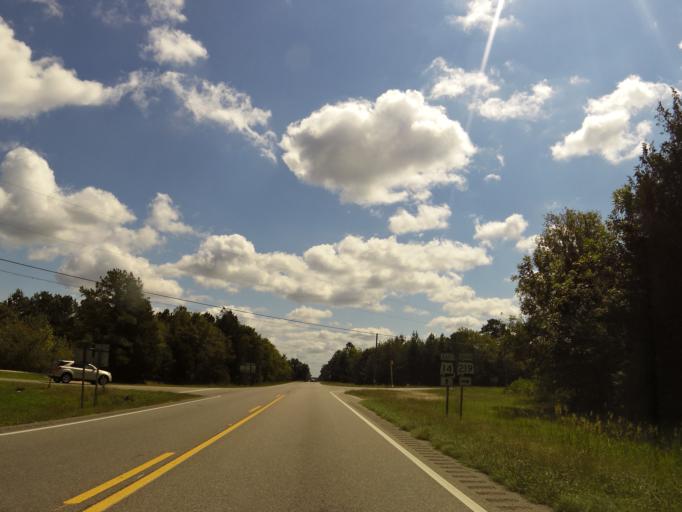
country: US
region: Alabama
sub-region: Dallas County
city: Selma
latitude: 32.4567
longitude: -87.0842
